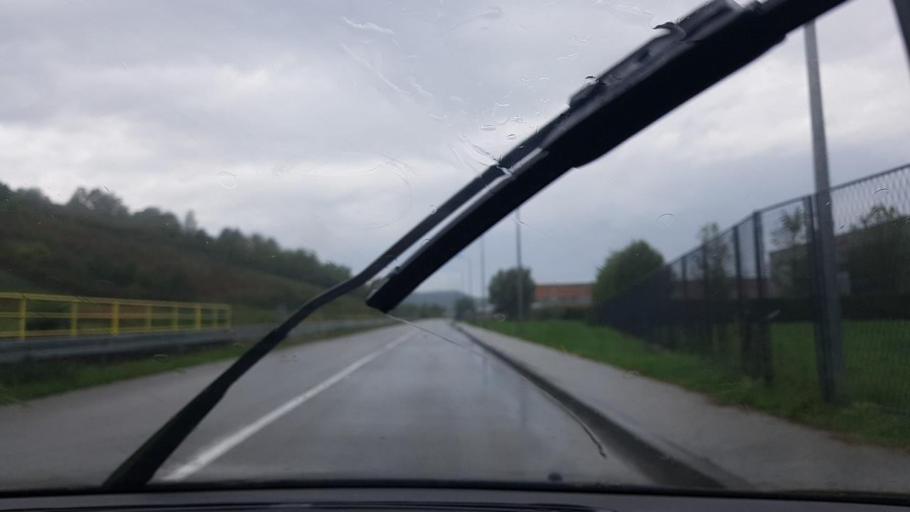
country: HR
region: Krapinsko-Zagorska
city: Zabok
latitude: 46.0682
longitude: 15.9083
